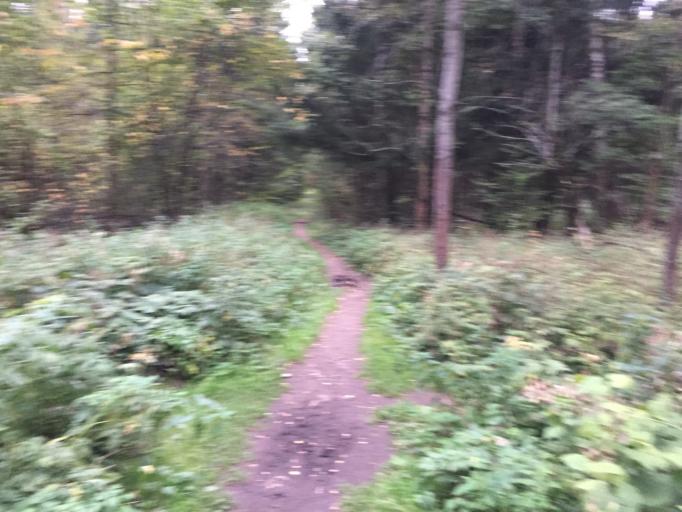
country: RU
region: Moscow
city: Babushkin
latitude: 55.8614
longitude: 37.7379
